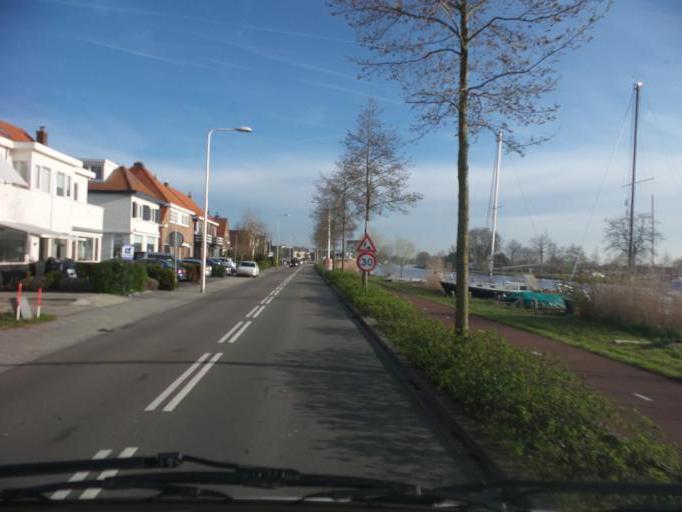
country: NL
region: South Holland
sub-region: Bodegraven-Reeuwijk
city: Reeuwijk
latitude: 52.0358
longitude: 4.7195
